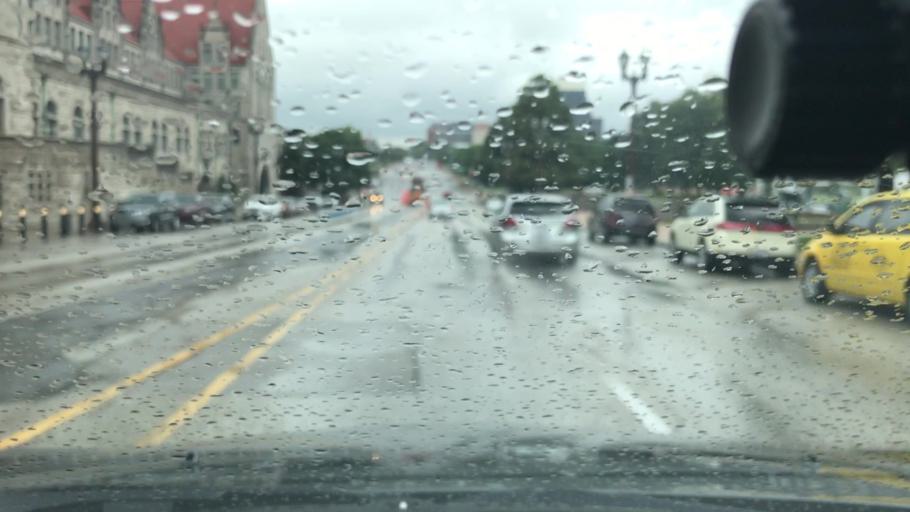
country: US
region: Missouri
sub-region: City of Saint Louis
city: St. Louis
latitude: 38.6294
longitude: -90.2068
